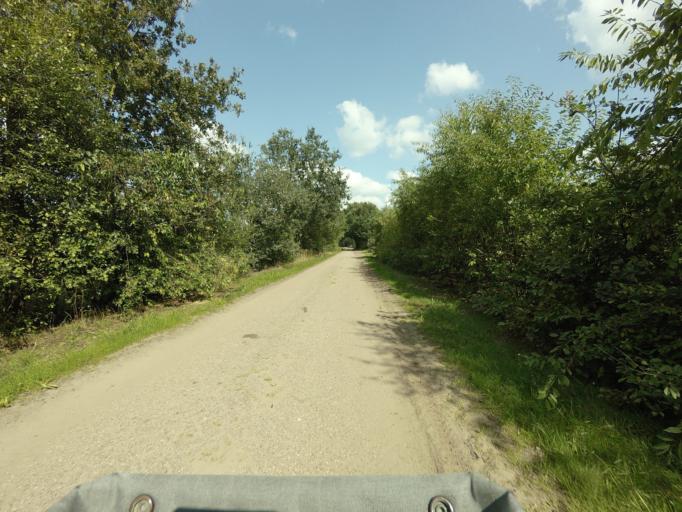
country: NL
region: Drenthe
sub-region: Gemeente Westerveld
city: Dwingeloo
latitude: 52.8812
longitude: 6.3853
